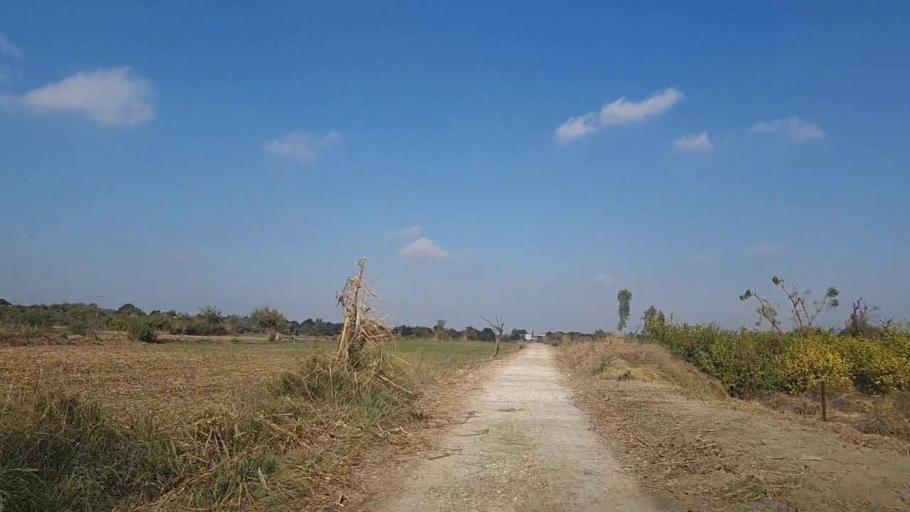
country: PK
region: Sindh
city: Tando Mittha Khan
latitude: 26.0039
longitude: 69.2595
